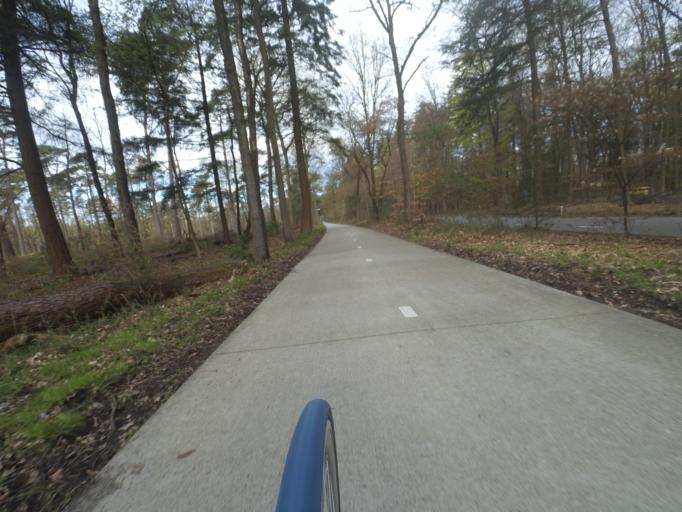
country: NL
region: Gelderland
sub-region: Gemeente Nunspeet
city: Nunspeet
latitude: 52.3388
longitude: 5.7974
